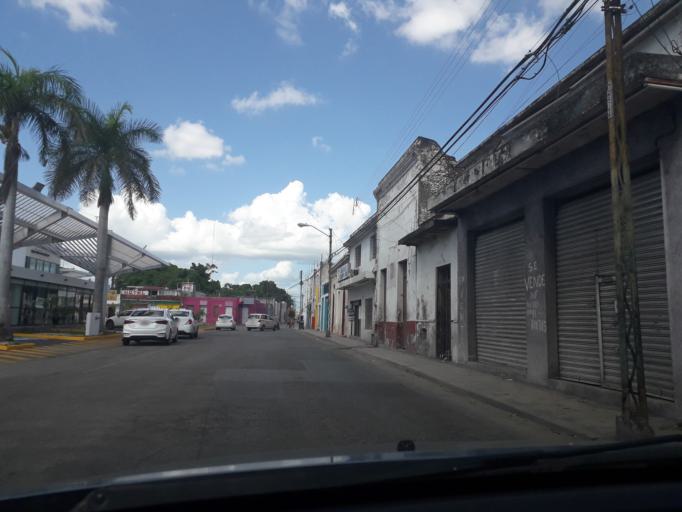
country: MX
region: Yucatan
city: Merida
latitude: 20.9622
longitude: -89.6293
